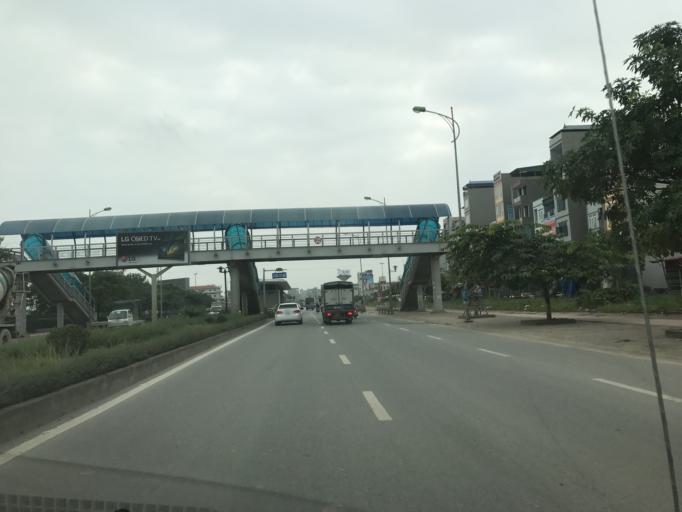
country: VN
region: Ha Noi
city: Ha Dong
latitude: 20.9674
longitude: 105.7562
